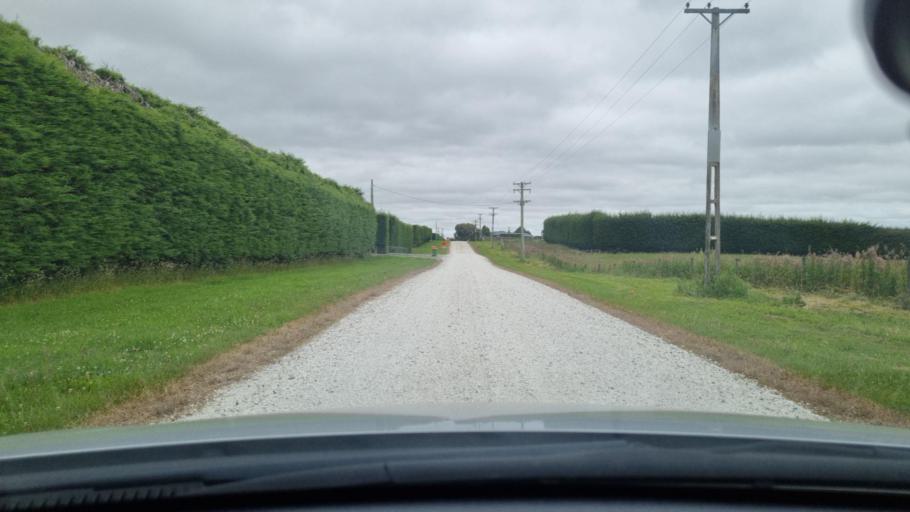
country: NZ
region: Southland
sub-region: Invercargill City
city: Invercargill
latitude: -46.3719
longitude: 168.3792
